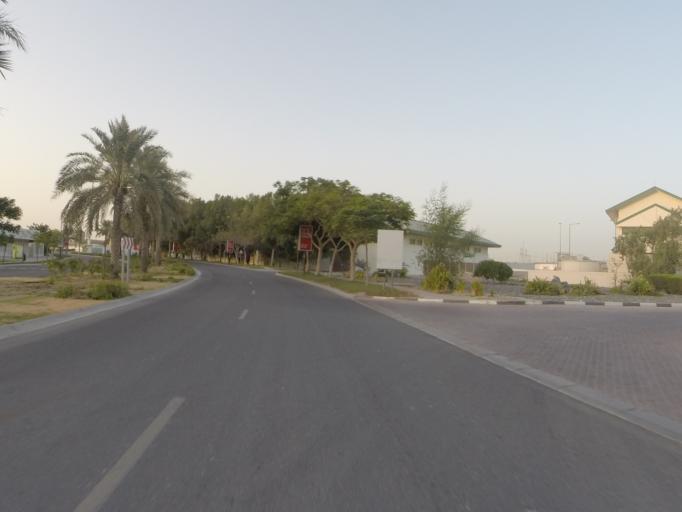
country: AE
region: Dubai
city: Dubai
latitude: 25.0625
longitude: 55.1434
